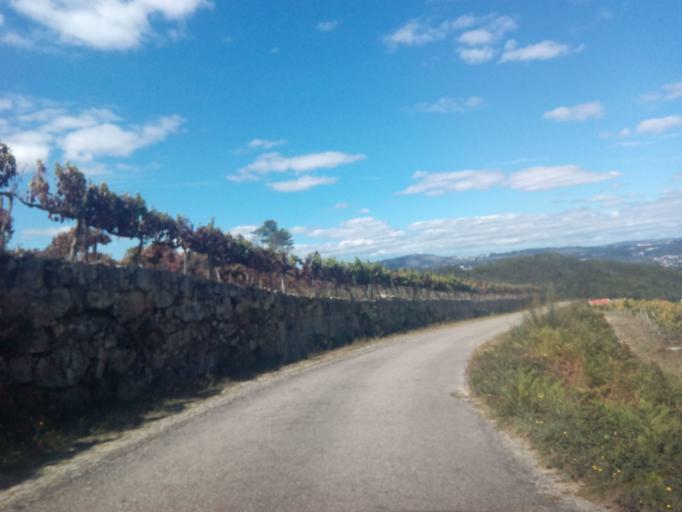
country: PT
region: Porto
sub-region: Paredes
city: Casteloes de Cepeda
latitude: 41.1528
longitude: -8.3141
